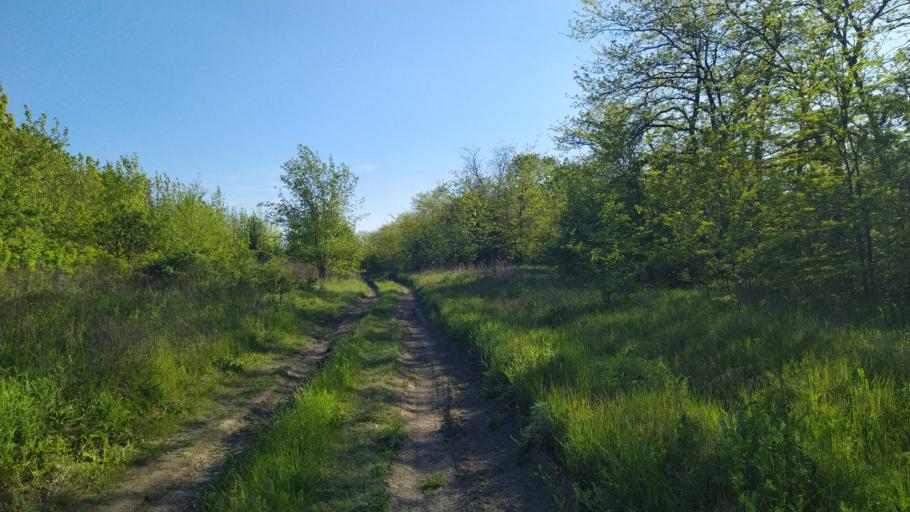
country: RU
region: Rostov
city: Bataysk
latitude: 47.0787
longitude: 39.7191
